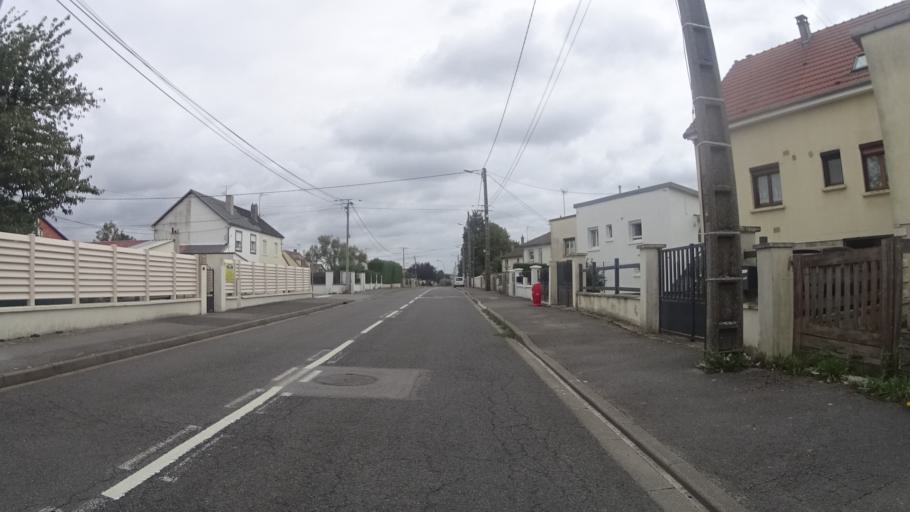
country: FR
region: Picardie
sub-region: Departement de l'Oise
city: Dreslincourt
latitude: 49.5080
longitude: 2.9304
